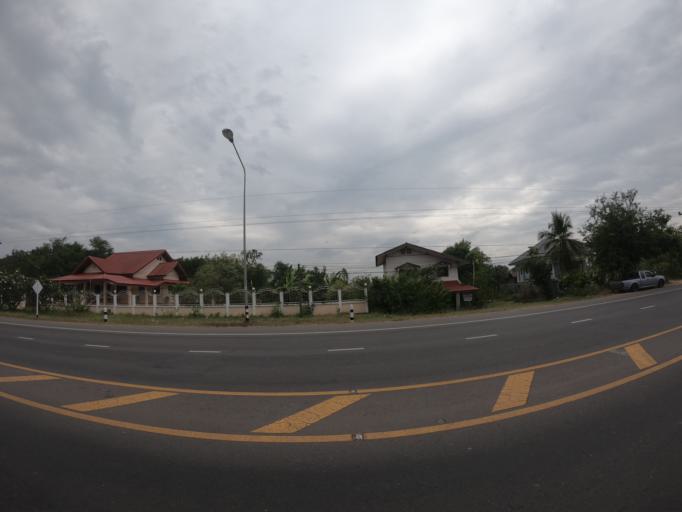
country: TH
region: Roi Et
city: Thawat Buri
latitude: 16.0830
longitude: 103.7433
